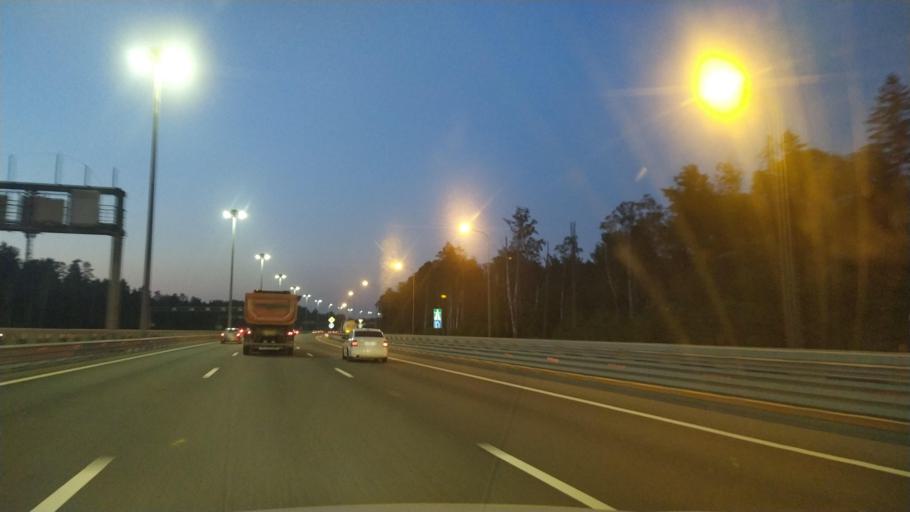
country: RU
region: St.-Petersburg
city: Levashovo
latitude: 60.0777
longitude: 30.1852
